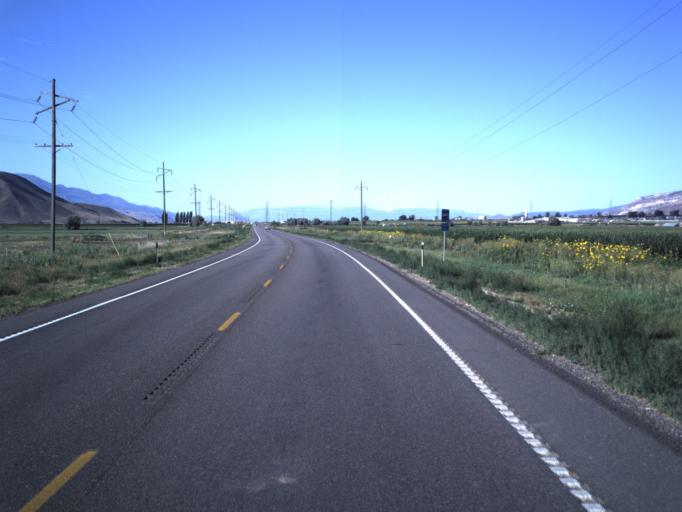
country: US
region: Utah
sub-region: Sevier County
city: Aurora
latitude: 38.9136
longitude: -111.9328
